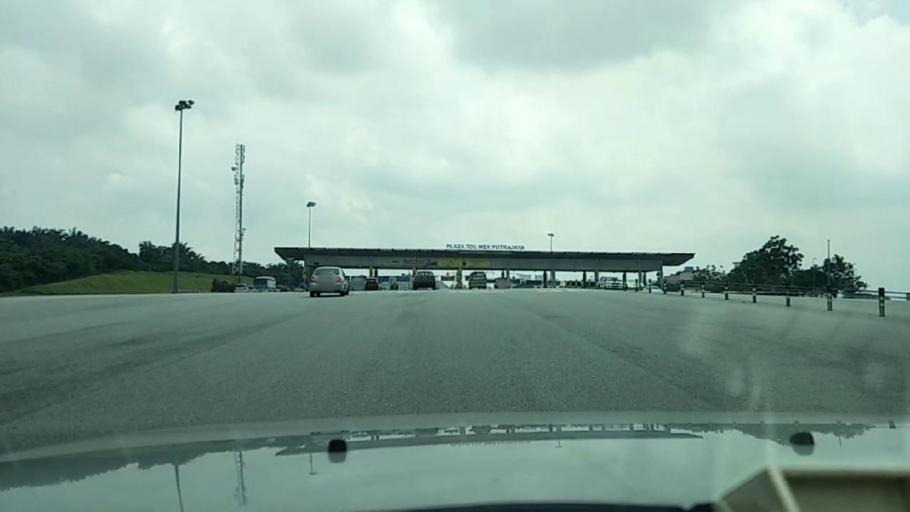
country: MY
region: Putrajaya
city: Putrajaya
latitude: 2.9484
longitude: 101.6516
